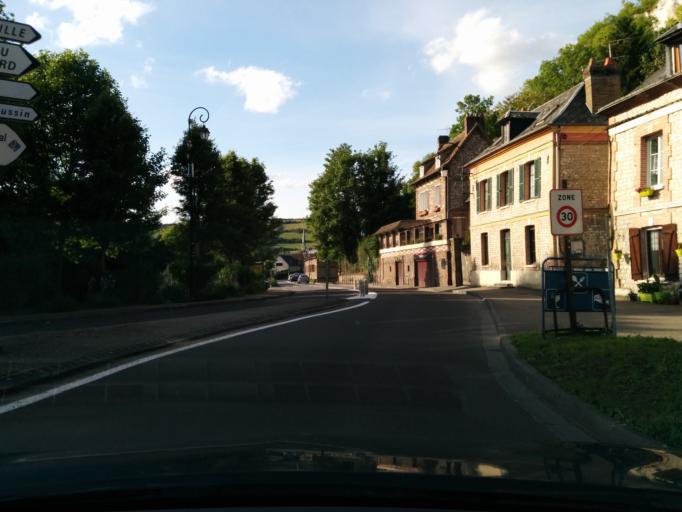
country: FR
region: Haute-Normandie
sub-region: Departement de l'Eure
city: Les Andelys
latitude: 49.2370
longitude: 1.4015
